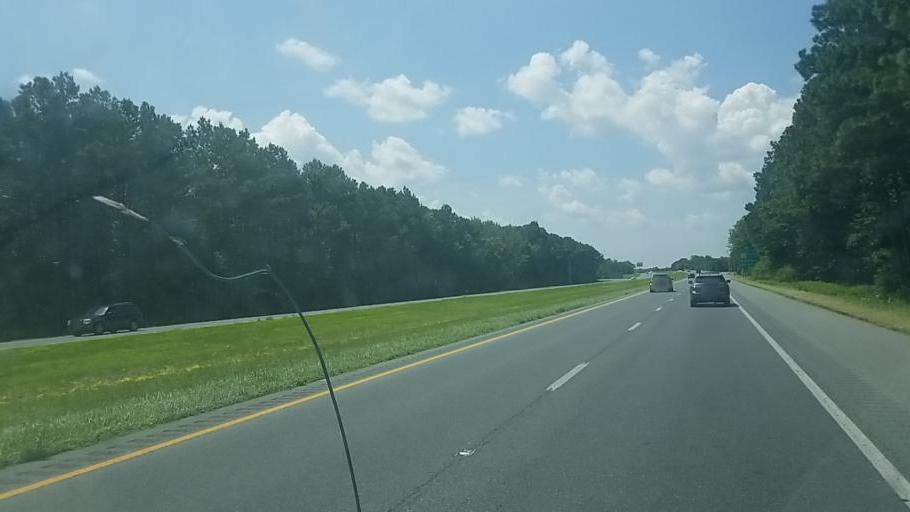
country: US
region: Maryland
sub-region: Wicomico County
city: Salisbury
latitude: 38.3370
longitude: -75.5618
